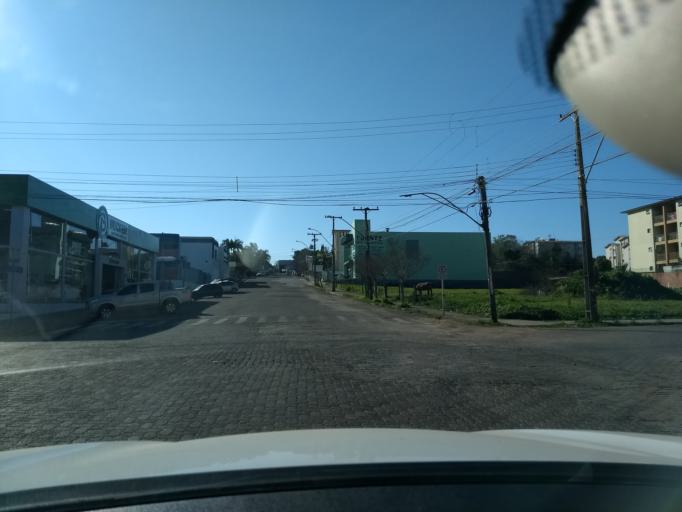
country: BR
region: Rio Grande do Sul
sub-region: Santa Cruz Do Sul
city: Santa Cruz do Sul
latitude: -29.7195
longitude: -52.4442
